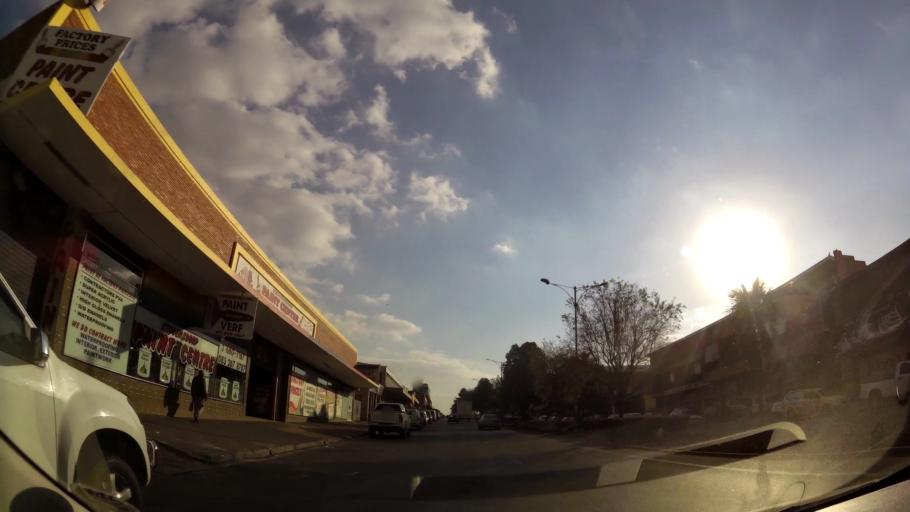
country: ZA
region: Gauteng
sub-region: West Rand District Municipality
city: Krugersdorp
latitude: -26.0981
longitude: 27.7511
